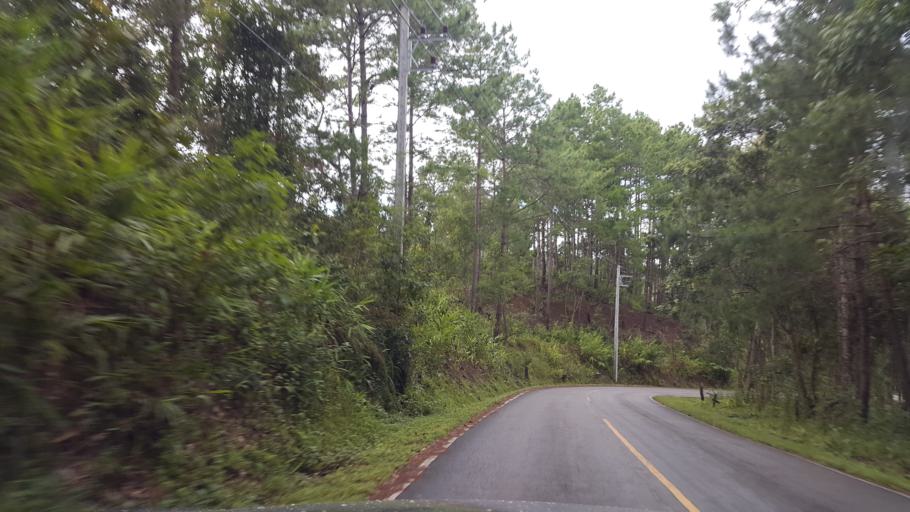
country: TH
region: Chiang Mai
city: Samoeng
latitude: 18.9013
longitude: 98.5010
